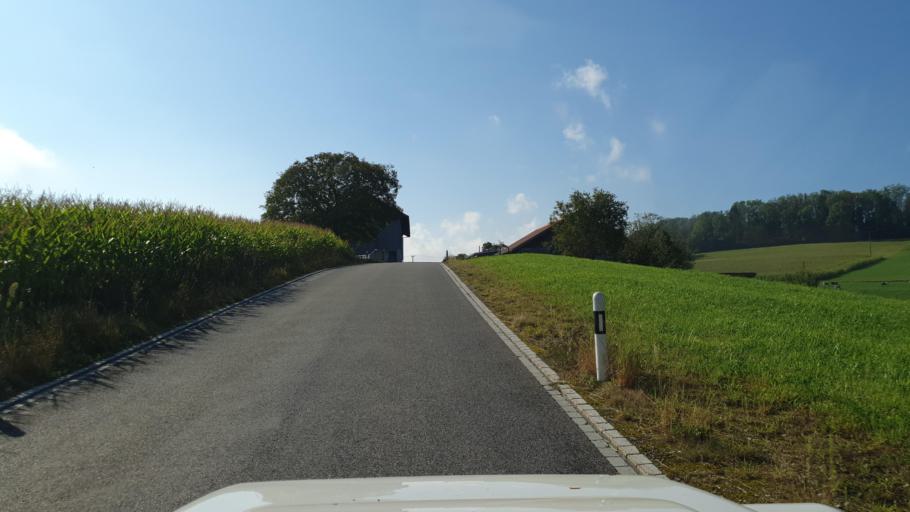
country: CH
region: Aargau
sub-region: Bezirk Muri
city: Waltenschwil
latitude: 47.3163
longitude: 8.2918
